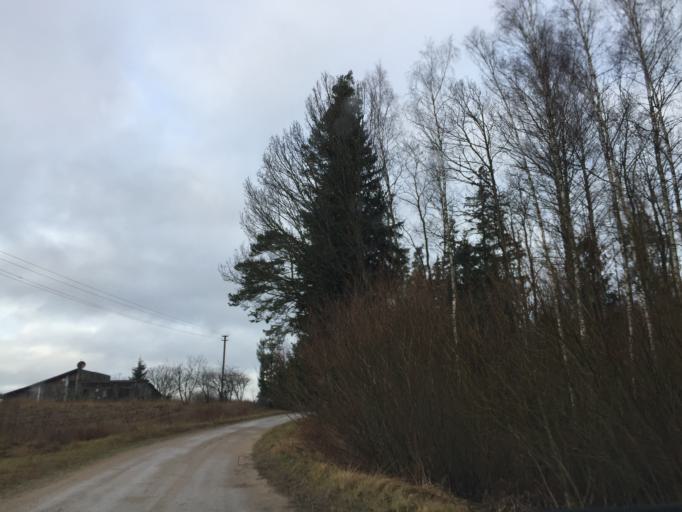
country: LV
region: Vainode
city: Vainode
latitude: 56.6051
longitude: 21.7999
